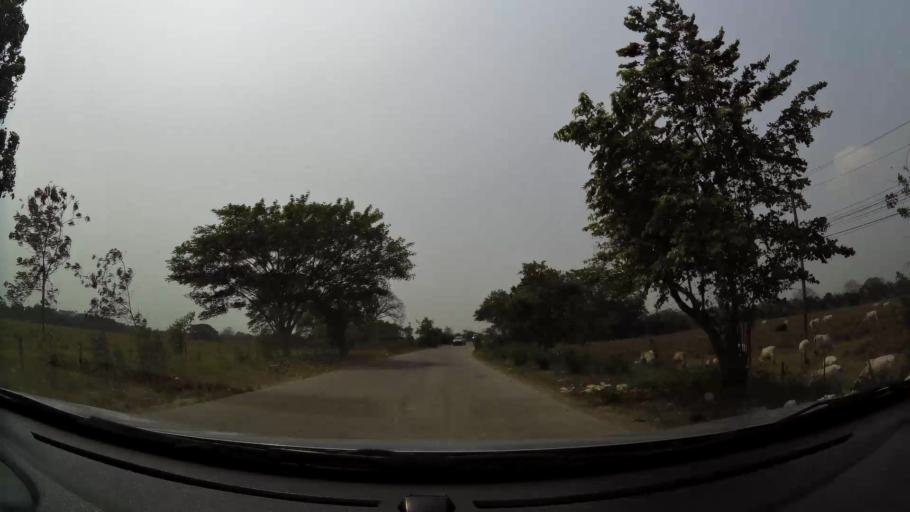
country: HN
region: Cortes
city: La Lima
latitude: 15.4237
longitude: -87.8977
